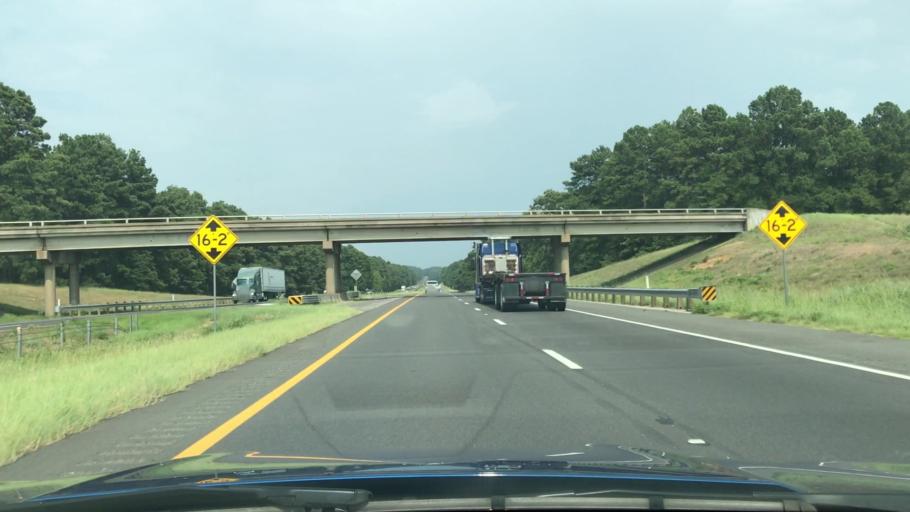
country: US
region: Texas
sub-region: Harrison County
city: Hallsville
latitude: 32.4666
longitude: -94.6223
